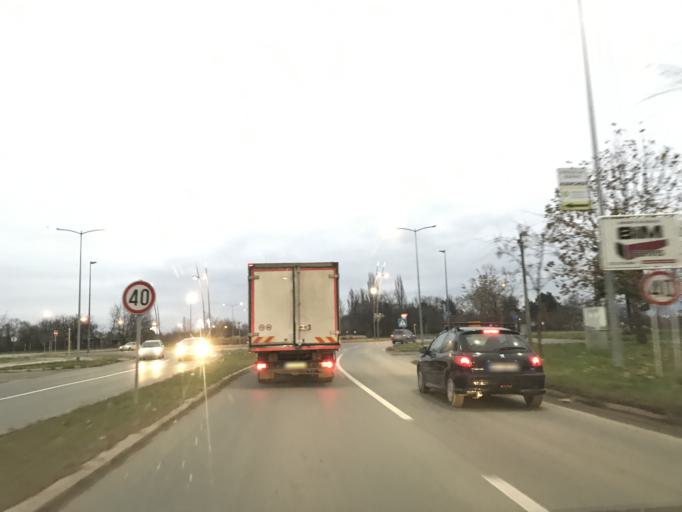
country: RS
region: Autonomna Pokrajina Vojvodina
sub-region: Juznobacki Okrug
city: Novi Sad
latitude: 45.2757
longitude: 19.8000
